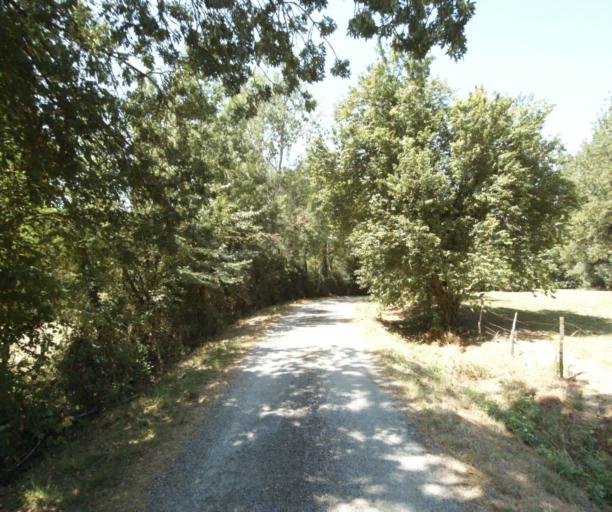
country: FR
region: Midi-Pyrenees
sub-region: Departement de la Haute-Garonne
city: Revel
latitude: 43.5031
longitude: 2.0234
